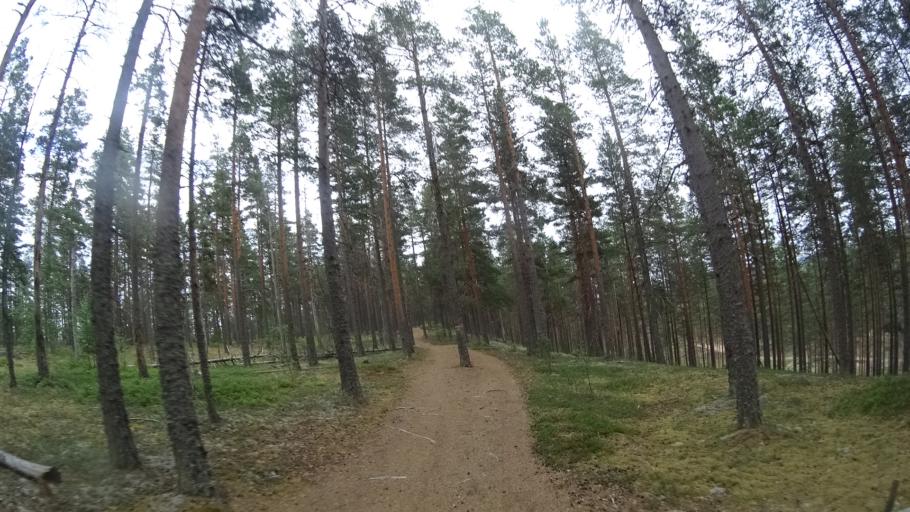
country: FI
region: Satakunta
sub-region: Pohjois-Satakunta
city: Jaemijaervi
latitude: 61.7741
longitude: 22.7278
